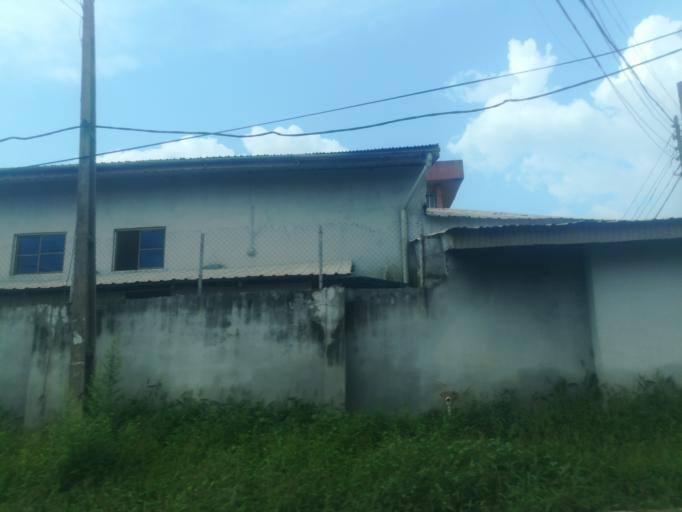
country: NG
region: Oyo
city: Ibadan
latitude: 7.3666
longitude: 3.8566
